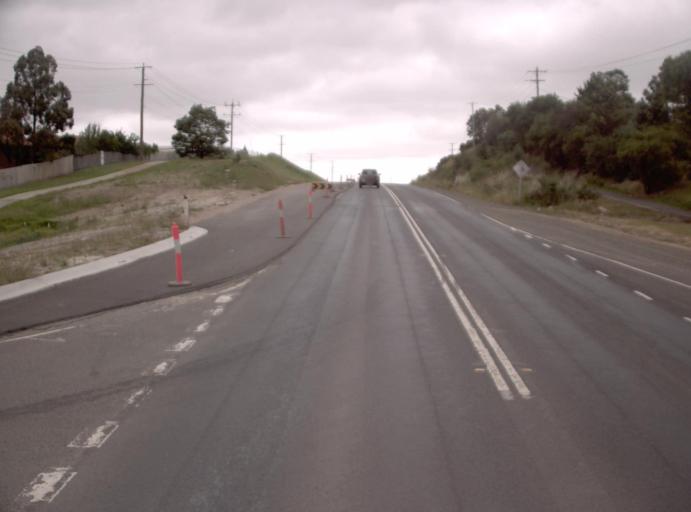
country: AU
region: Victoria
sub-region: Casey
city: Hallam
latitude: -38.0244
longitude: 145.2696
